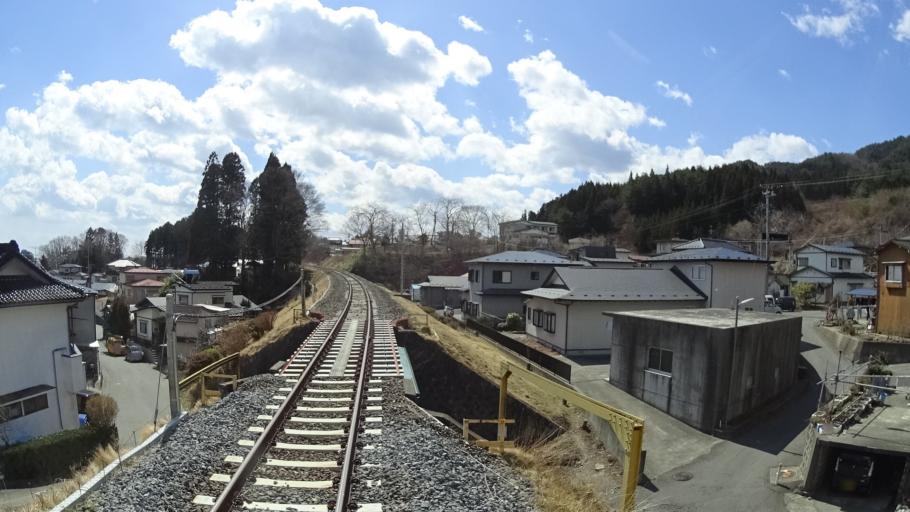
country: JP
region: Iwate
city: Yamada
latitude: 39.4258
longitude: 141.9720
